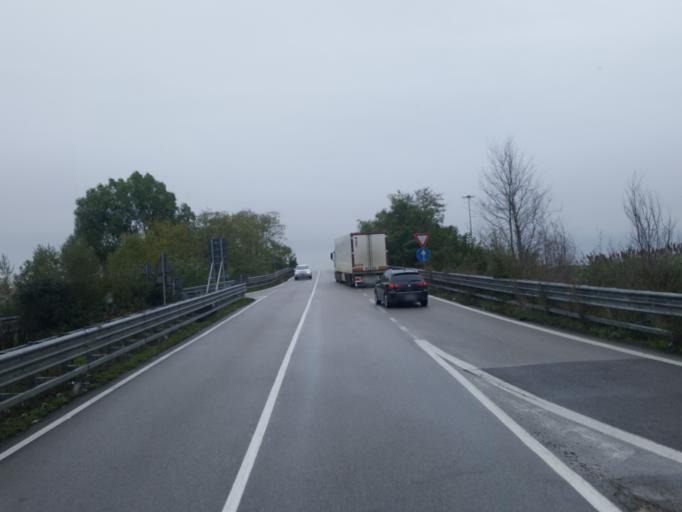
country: IT
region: Veneto
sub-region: Provincia di Rovigo
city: Villamarzana
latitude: 45.0184
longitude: 11.7021
